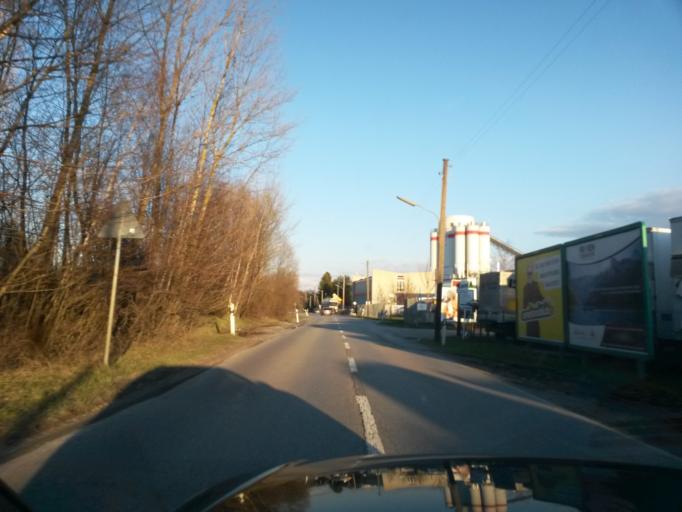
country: DE
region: Bavaria
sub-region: Upper Bavaria
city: Karlsfeld
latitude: 48.1964
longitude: 11.4835
